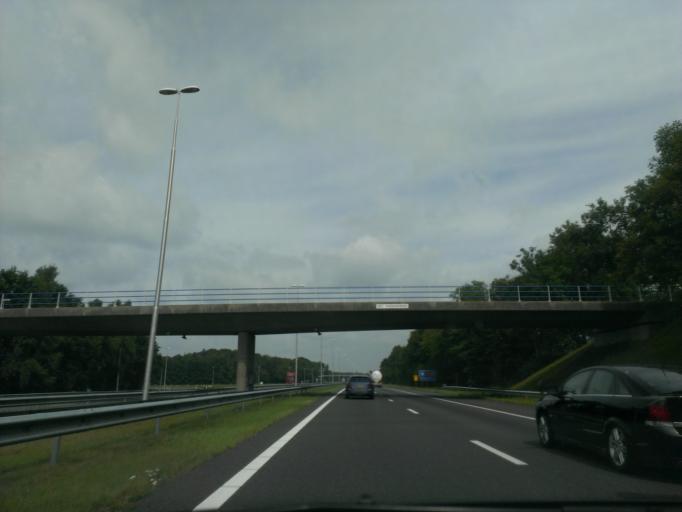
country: NL
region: Gelderland
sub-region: Gemeente Epe
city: Epe
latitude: 52.3294
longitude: 6.0078
